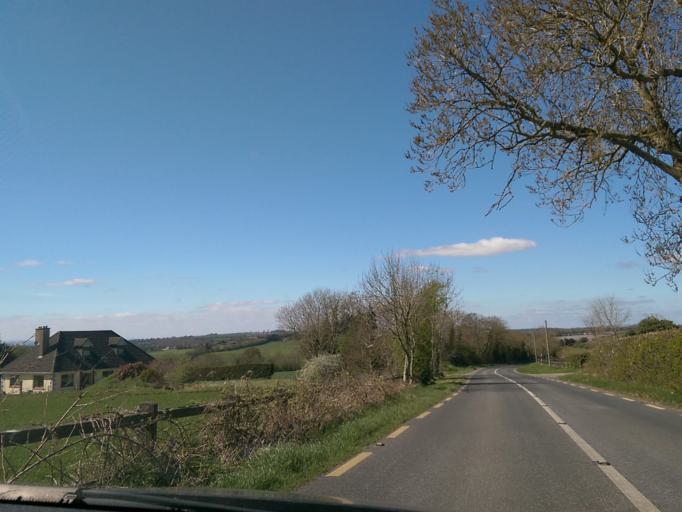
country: IE
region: Leinster
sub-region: Kildare
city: Moone
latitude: 52.9838
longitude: -6.7824
